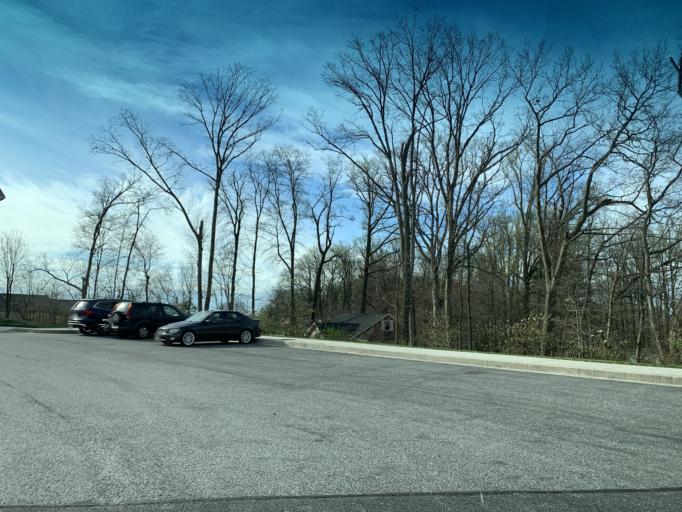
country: US
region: Maryland
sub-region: Harford County
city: South Bel Air
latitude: 39.5663
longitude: -76.3296
